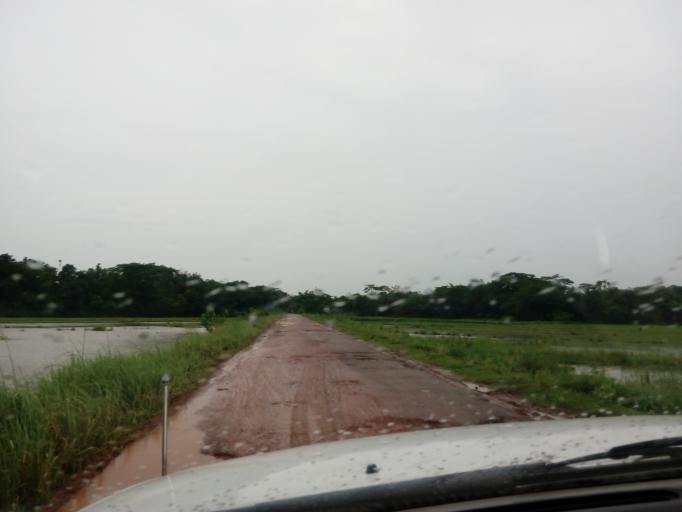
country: BD
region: Sylhet
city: Sylhet
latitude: 24.9632
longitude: 91.7948
